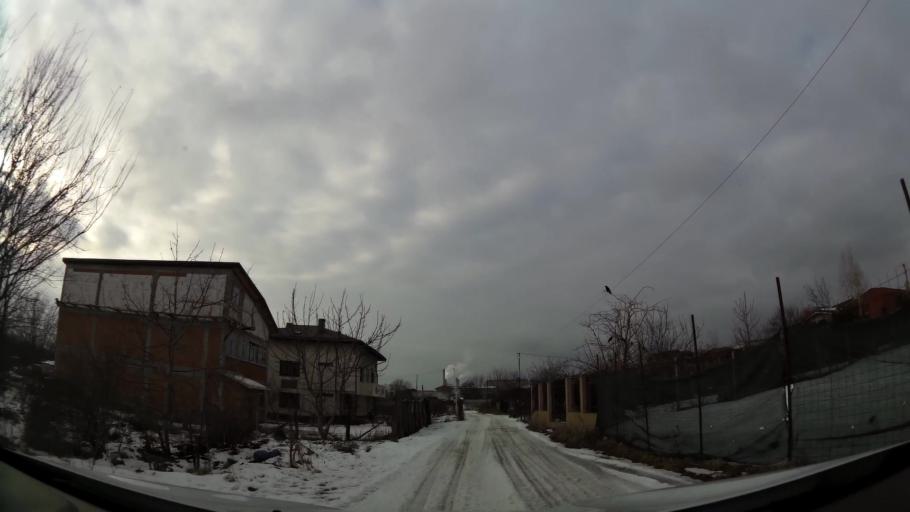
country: RO
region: Ilfov
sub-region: Comuna Popesti-Leordeni
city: Popesti-Leordeni
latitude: 44.4005
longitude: 26.1786
